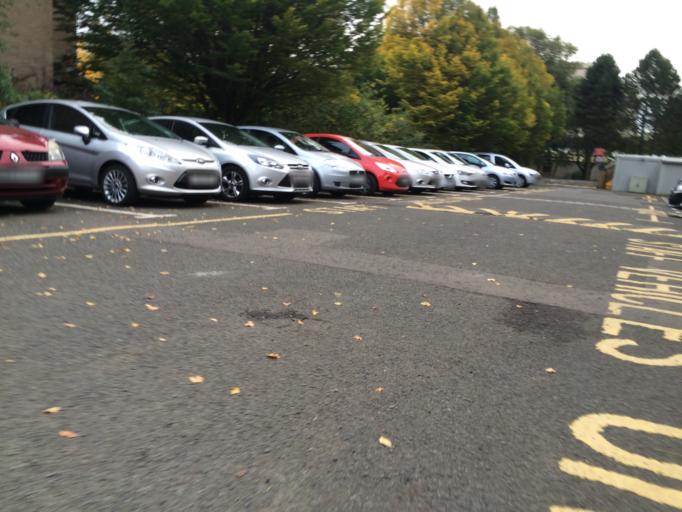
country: GB
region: Scotland
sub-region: Edinburgh
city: Edinburgh
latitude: 55.9244
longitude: -3.1786
